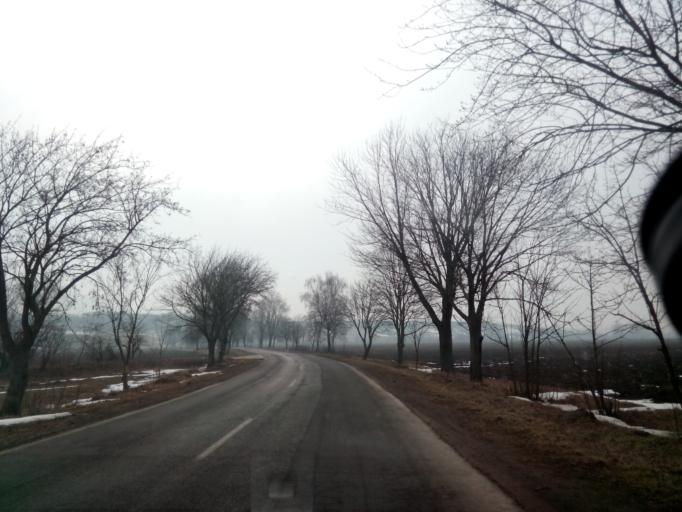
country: HU
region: Borsod-Abauj-Zemplen
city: Gonc
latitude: 48.4852
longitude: 21.2531
